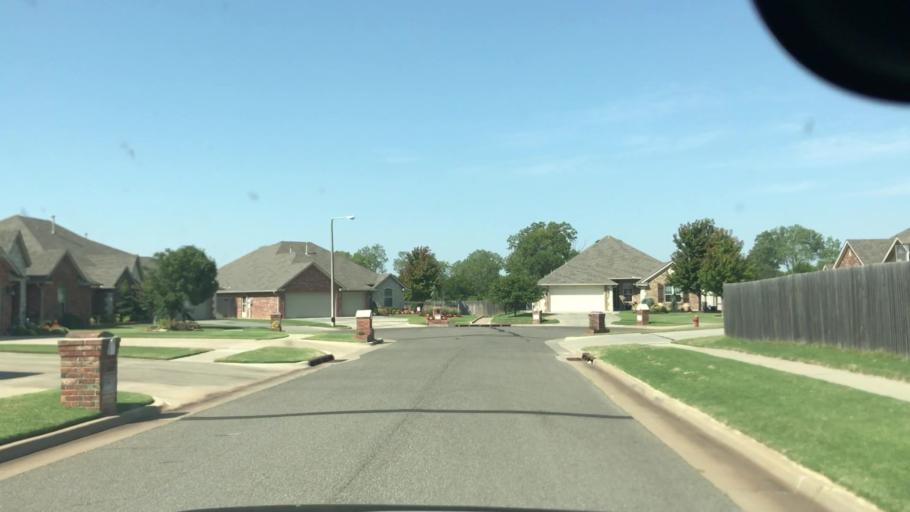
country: US
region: Oklahoma
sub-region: Cleveland County
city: Moore
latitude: 35.3513
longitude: -97.5160
